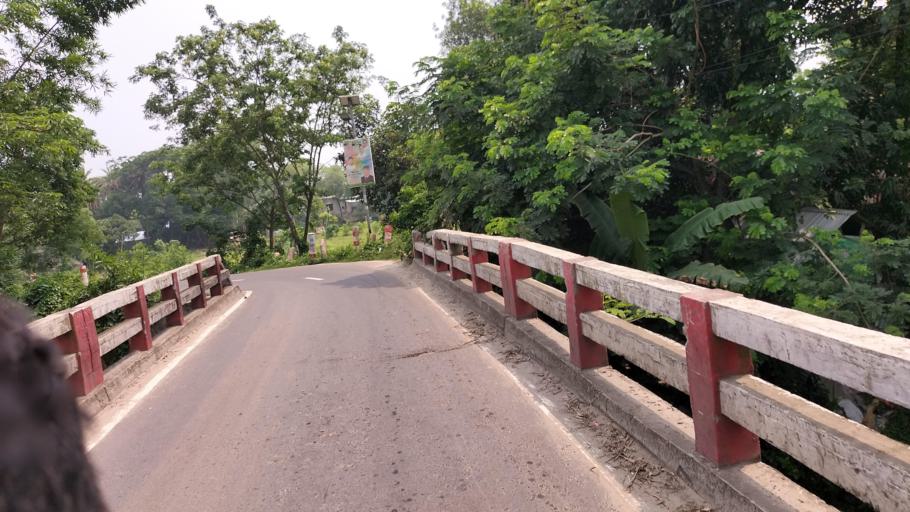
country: BD
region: Dhaka
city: Azimpur
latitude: 23.7203
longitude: 90.2760
